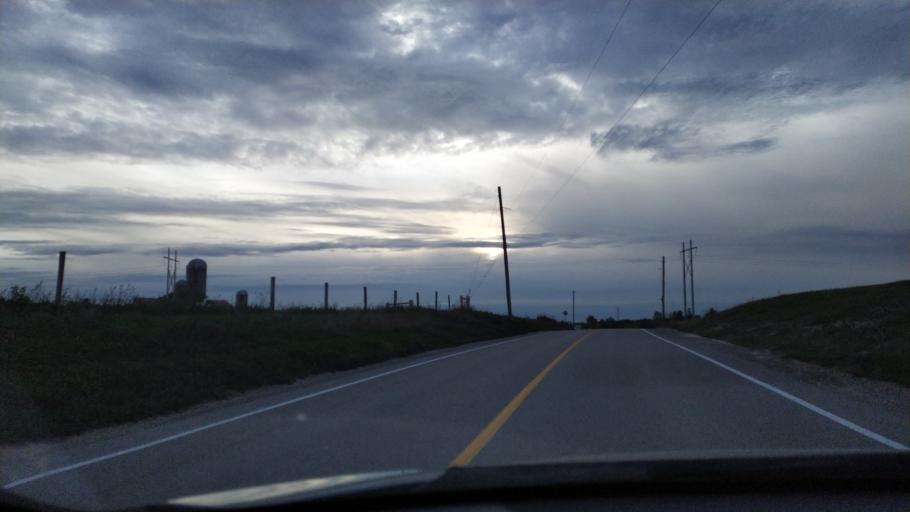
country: CA
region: Ontario
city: Waterloo
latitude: 43.4959
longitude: -80.5908
